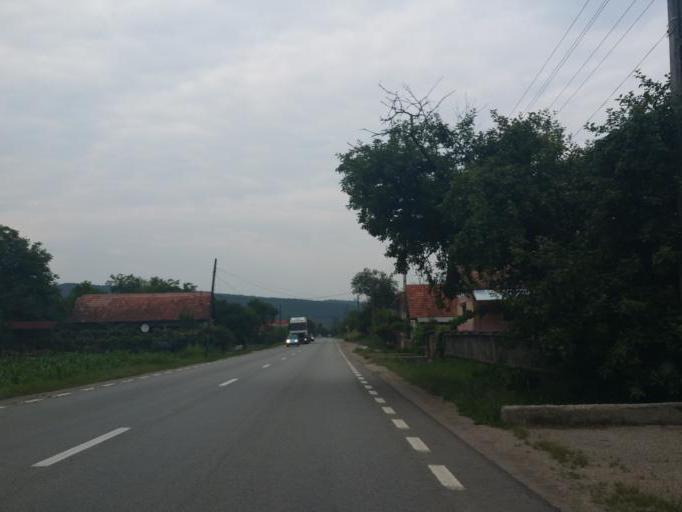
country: RO
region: Salaj
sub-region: Comuna Zimbor
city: Zimbor
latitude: 46.9807
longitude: 23.2524
